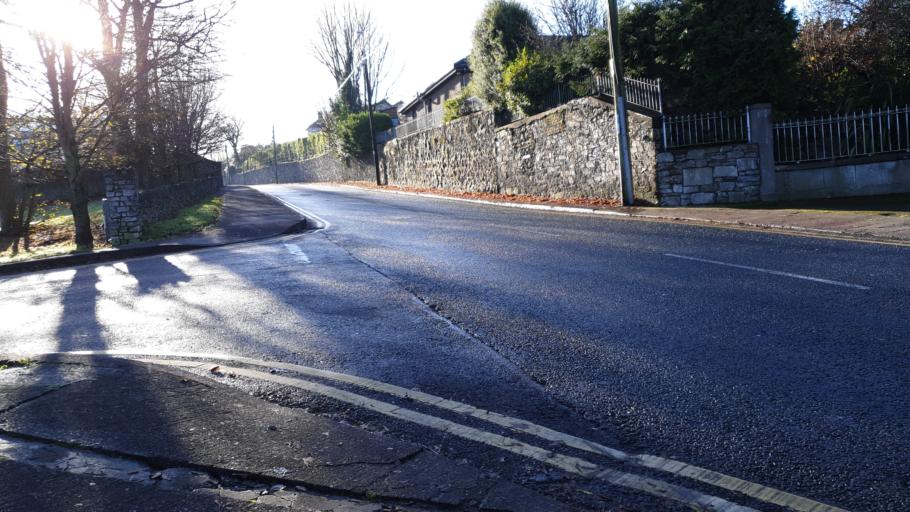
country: IE
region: Munster
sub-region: County Cork
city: Cork
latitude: 51.8934
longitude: -8.4336
